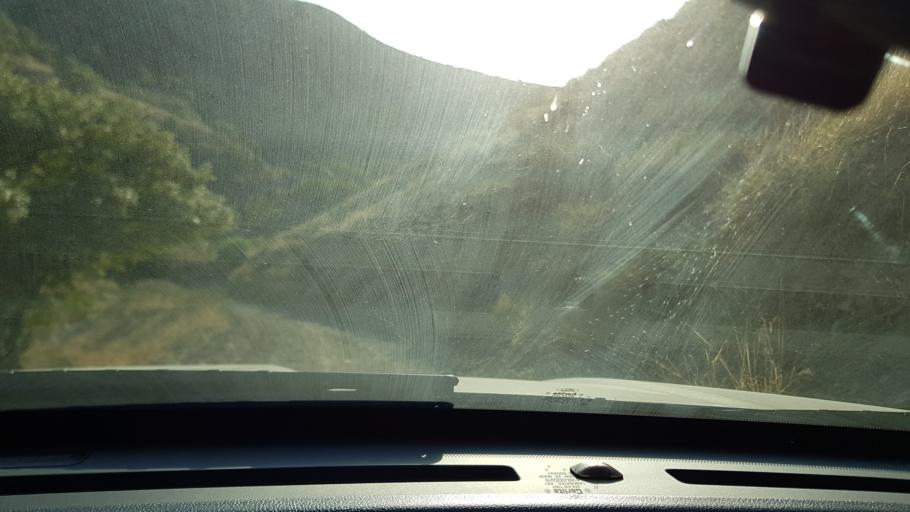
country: TM
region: Ahal
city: Baharly
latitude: 38.4047
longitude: 56.9064
